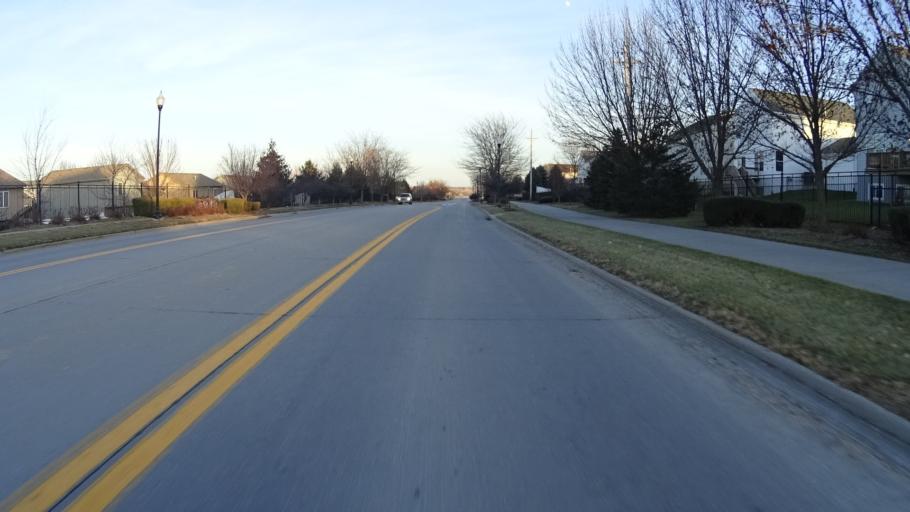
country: US
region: Nebraska
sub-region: Sarpy County
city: Papillion
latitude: 41.1326
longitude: -96.0570
